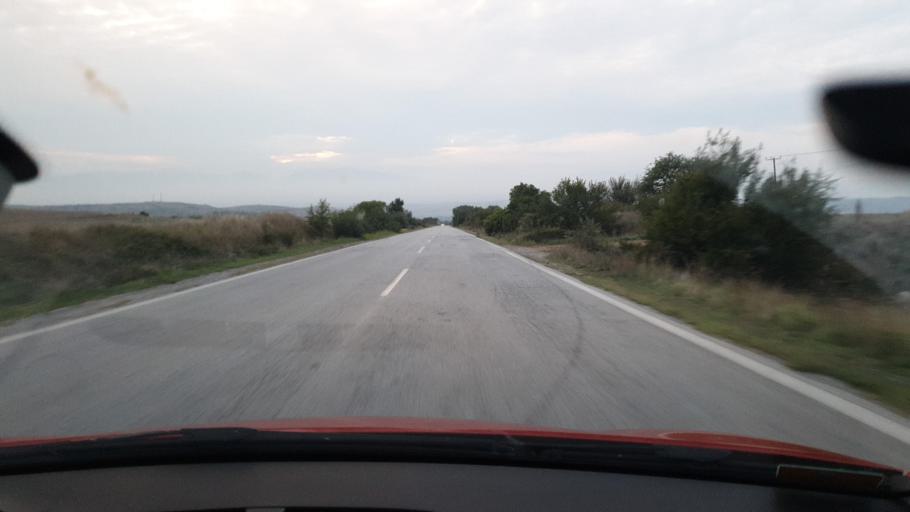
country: GR
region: Central Macedonia
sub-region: Nomos Kilkis
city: Polykastro
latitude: 41.0075
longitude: 22.6937
